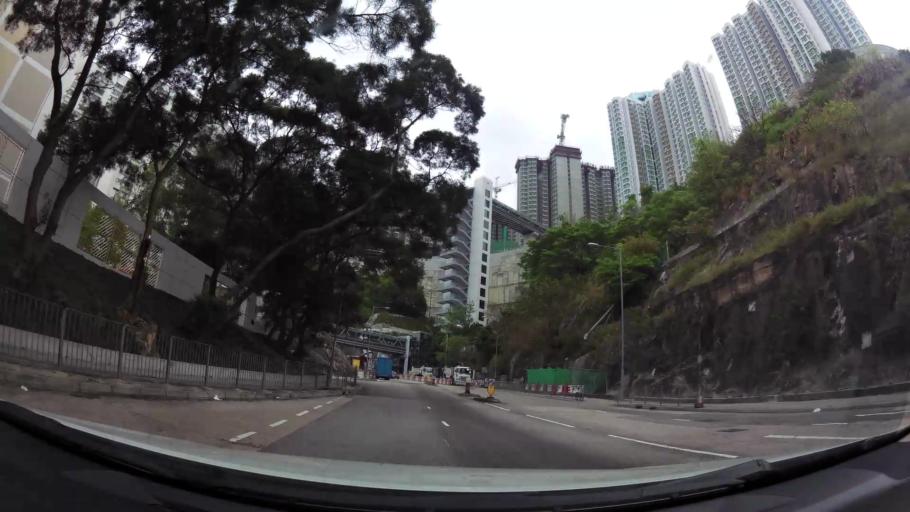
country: HK
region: Kowloon City
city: Kowloon
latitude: 22.3247
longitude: 114.2290
